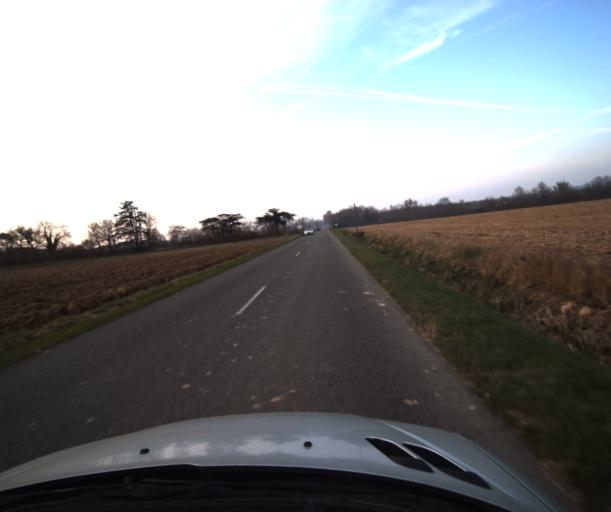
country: FR
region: Midi-Pyrenees
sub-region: Departement du Tarn-et-Garonne
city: Labastide-Saint-Pierre
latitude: 43.8960
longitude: 1.3717
